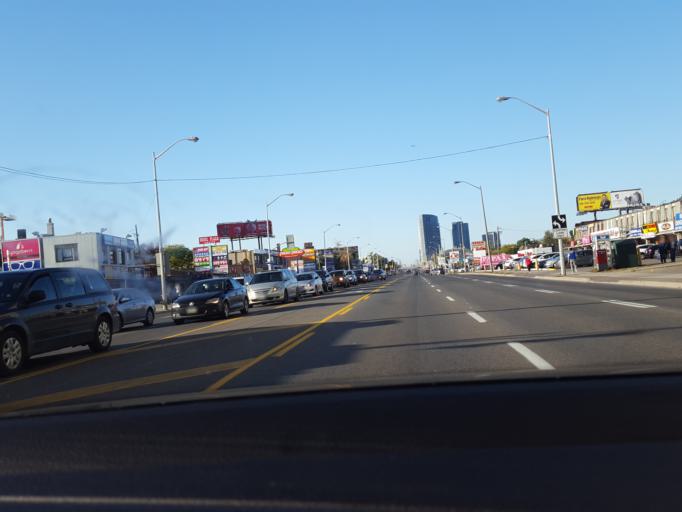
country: CA
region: Ontario
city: North York
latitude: 43.7903
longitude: -79.4181
